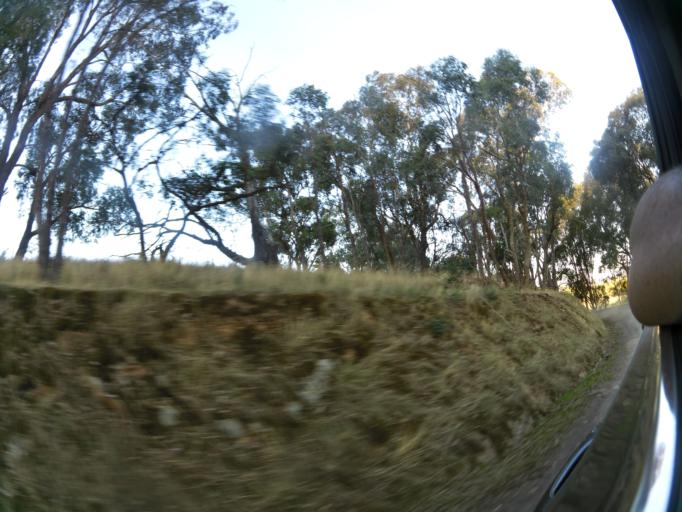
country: AU
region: Victoria
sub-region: Murrindindi
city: Alexandra
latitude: -37.1485
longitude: 145.5211
